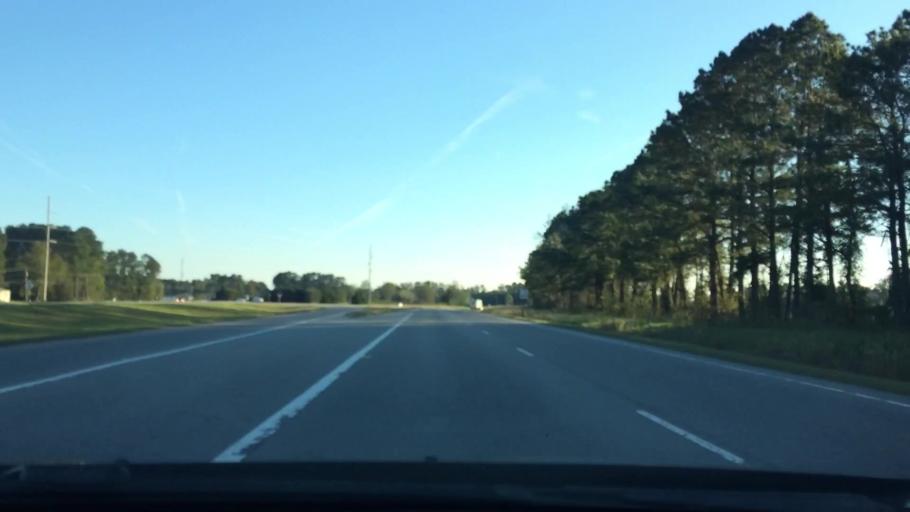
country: US
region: North Carolina
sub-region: Pitt County
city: Grifton
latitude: 35.4067
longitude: -77.4360
